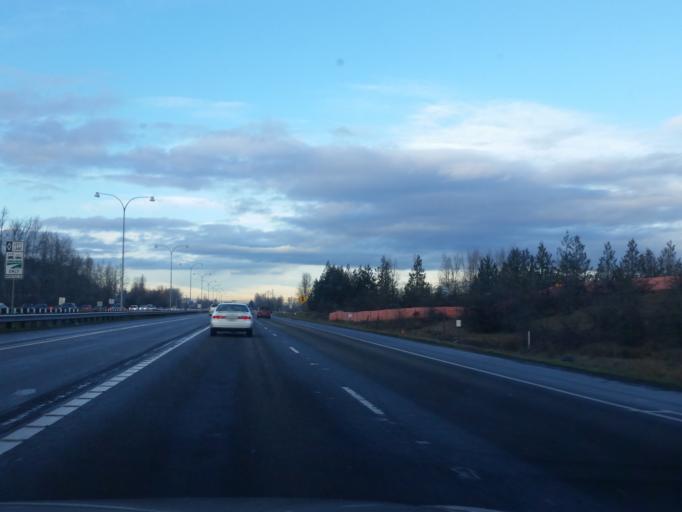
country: US
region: Washington
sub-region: King County
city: Auburn
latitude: 47.3225
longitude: -122.2448
